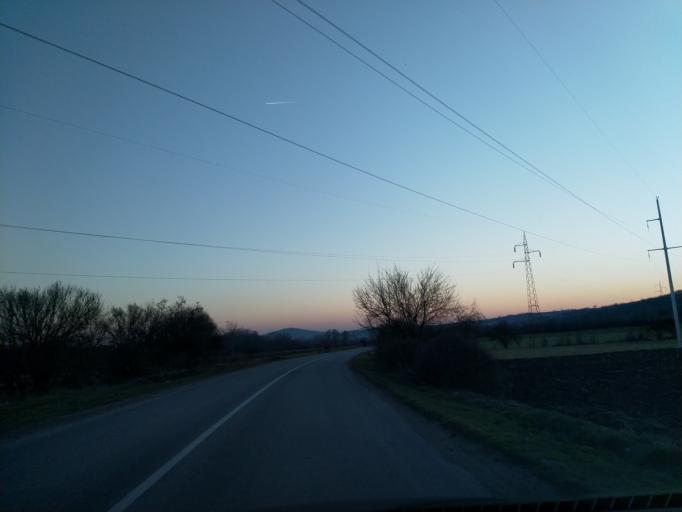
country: RS
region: Central Serbia
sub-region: Pomoravski Okrug
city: Paracin
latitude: 43.9009
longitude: 21.4948
